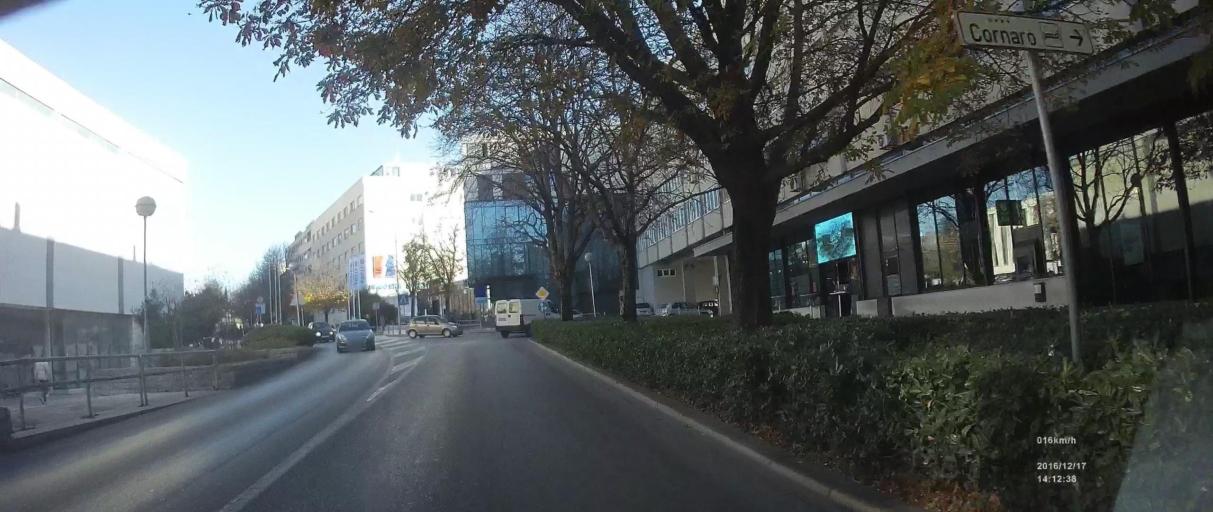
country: HR
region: Splitsko-Dalmatinska
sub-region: Grad Split
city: Split
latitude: 43.5143
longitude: 16.4400
